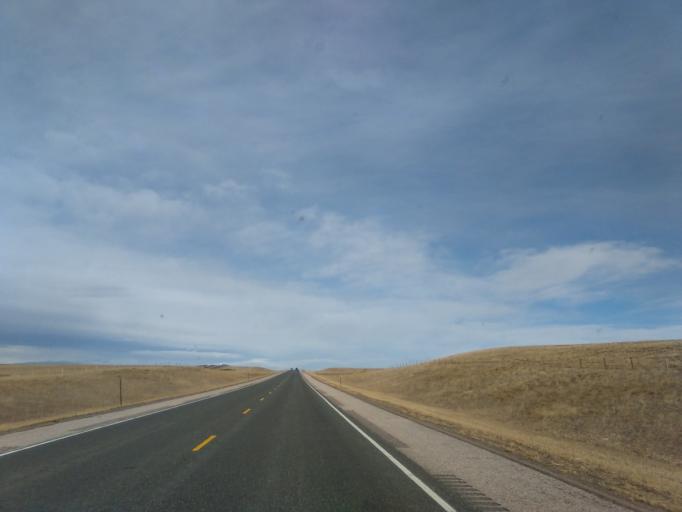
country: US
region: Wyoming
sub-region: Laramie County
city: Pine Bluffs
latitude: 41.5868
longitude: -104.2690
